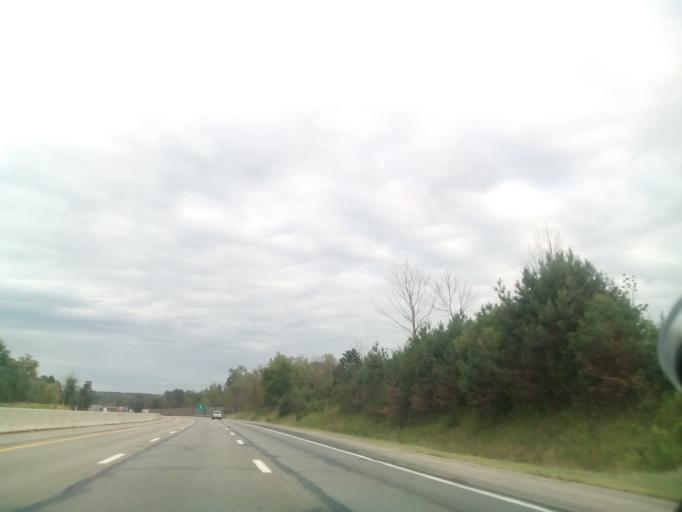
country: US
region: Ohio
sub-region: Cuyahoga County
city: Broadview Heights
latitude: 41.2842
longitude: -81.6572
